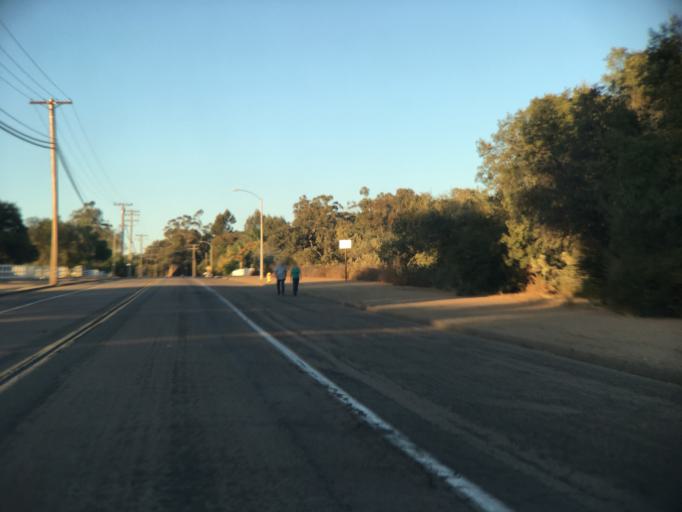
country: US
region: California
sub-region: San Diego County
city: Alpine
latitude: 32.8119
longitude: -116.7784
